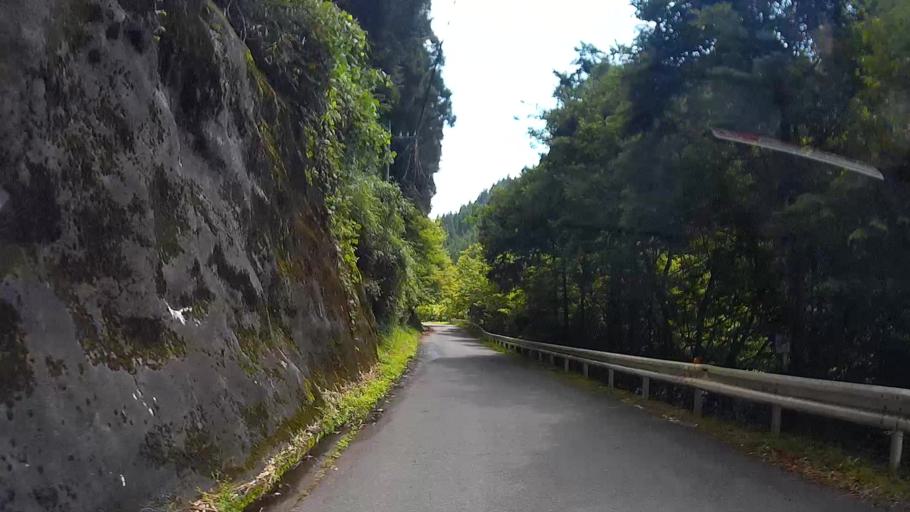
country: JP
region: Saitama
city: Chichibu
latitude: 35.9089
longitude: 139.0927
